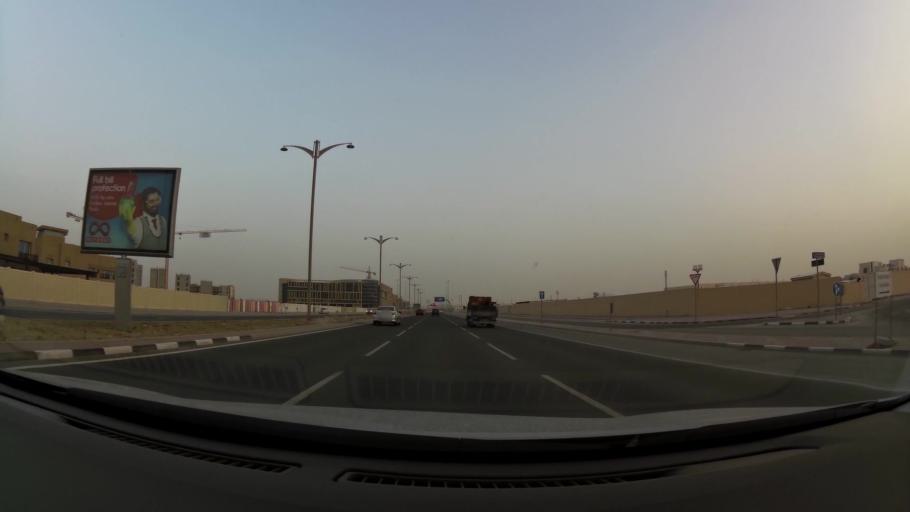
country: QA
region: Baladiyat ar Rayyan
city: Ar Rayyan
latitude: 25.2568
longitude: 51.4680
